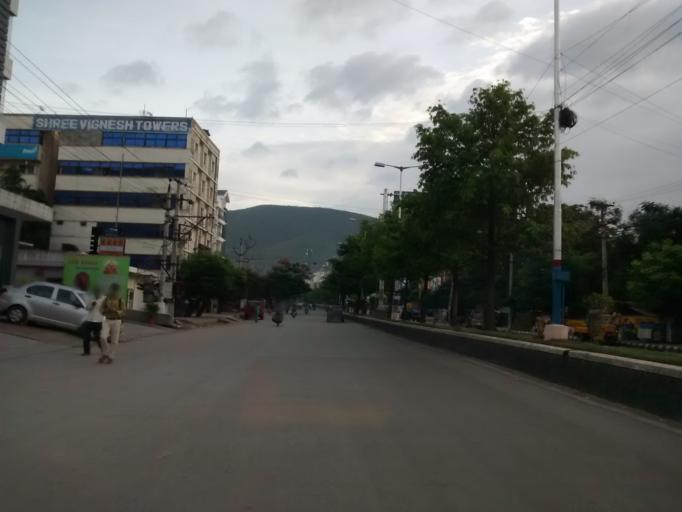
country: IN
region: Andhra Pradesh
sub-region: Chittoor
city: Akkarampalle
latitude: 13.6429
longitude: 79.4276
